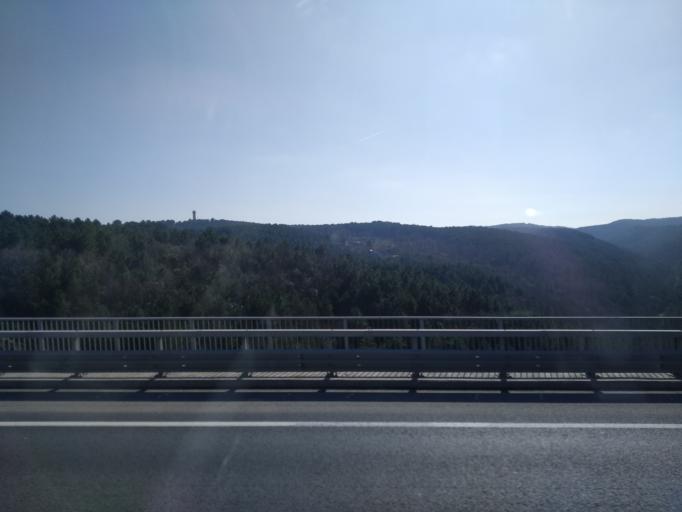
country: TR
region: Istanbul
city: Mahmut Sevket Pasa
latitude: 41.1975
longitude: 29.1395
